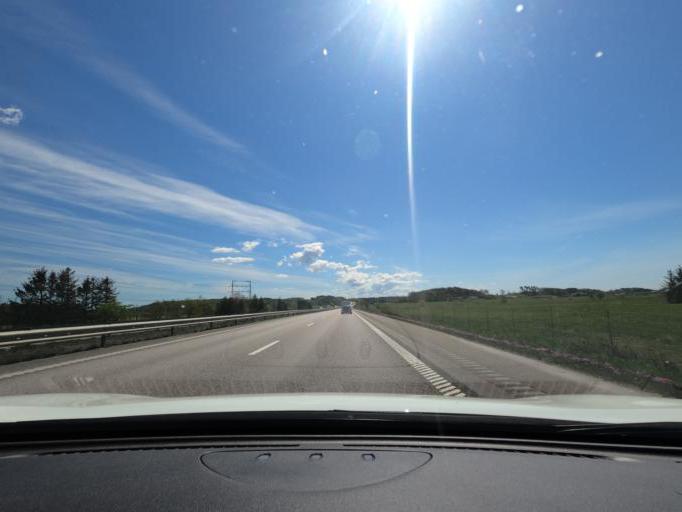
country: SE
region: Halland
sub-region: Kungsbacka Kommun
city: Kungsbacka
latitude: 57.4622
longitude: 12.0776
